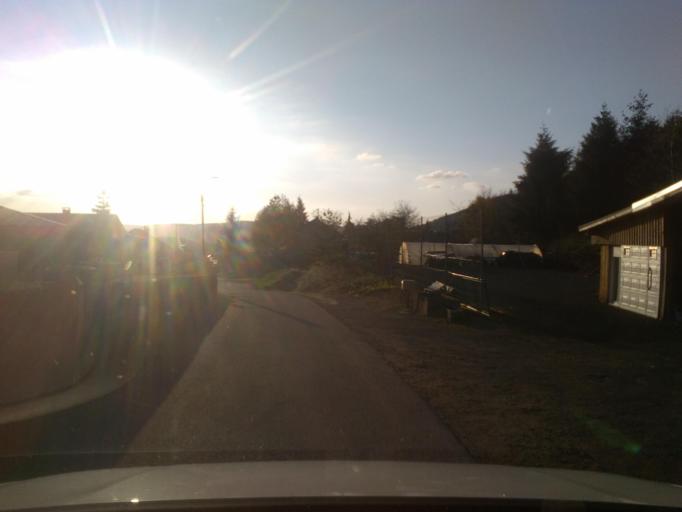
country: FR
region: Lorraine
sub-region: Departement des Vosges
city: Saint-Die-des-Vosges
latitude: 48.3191
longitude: 6.9736
